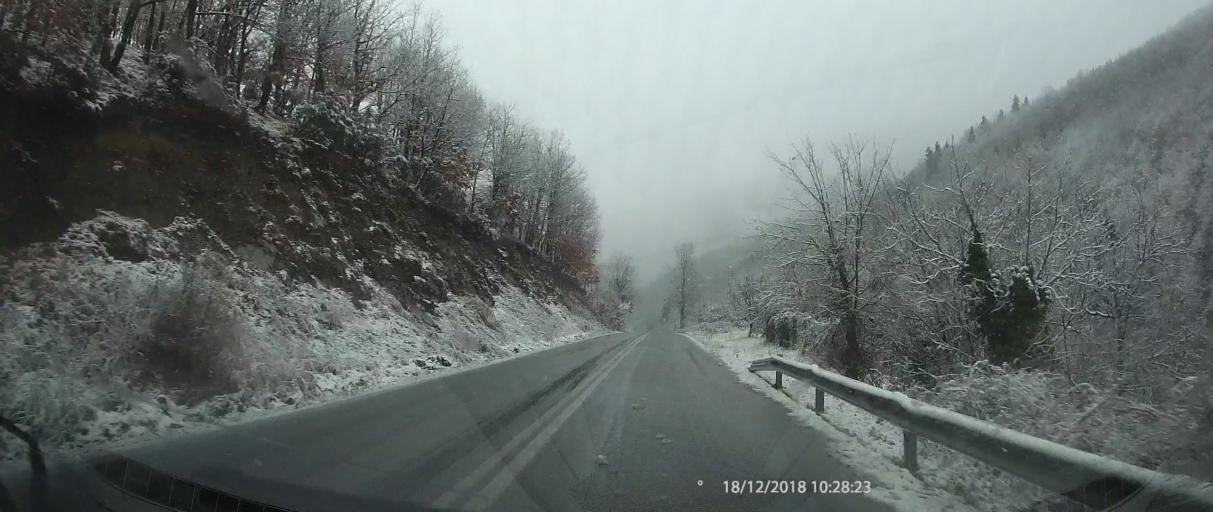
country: GR
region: Central Macedonia
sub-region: Nomos Pierias
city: Kato Milia
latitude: 40.1780
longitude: 22.2609
